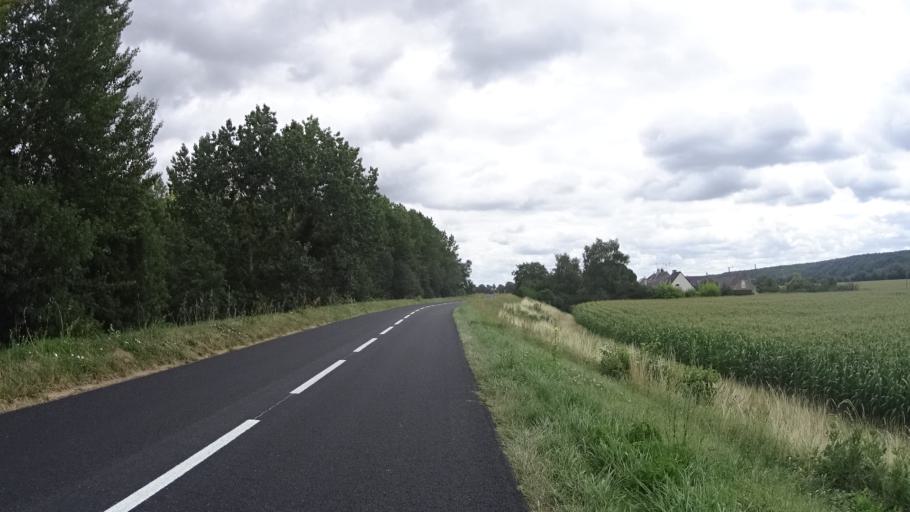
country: FR
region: Centre
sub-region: Departement d'Indre-et-Loire
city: Huismes
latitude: 47.2624
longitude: 0.2924
